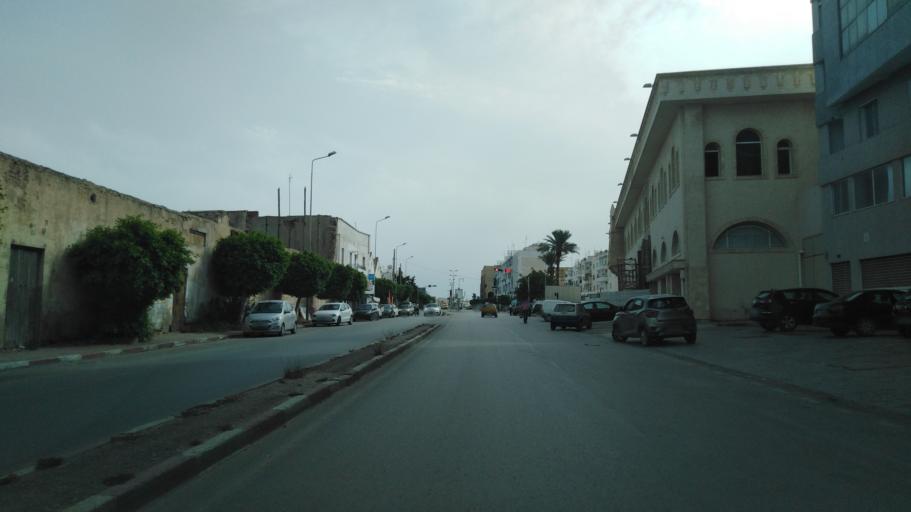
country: TN
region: Safaqis
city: Sfax
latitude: 34.7426
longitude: 10.7628
